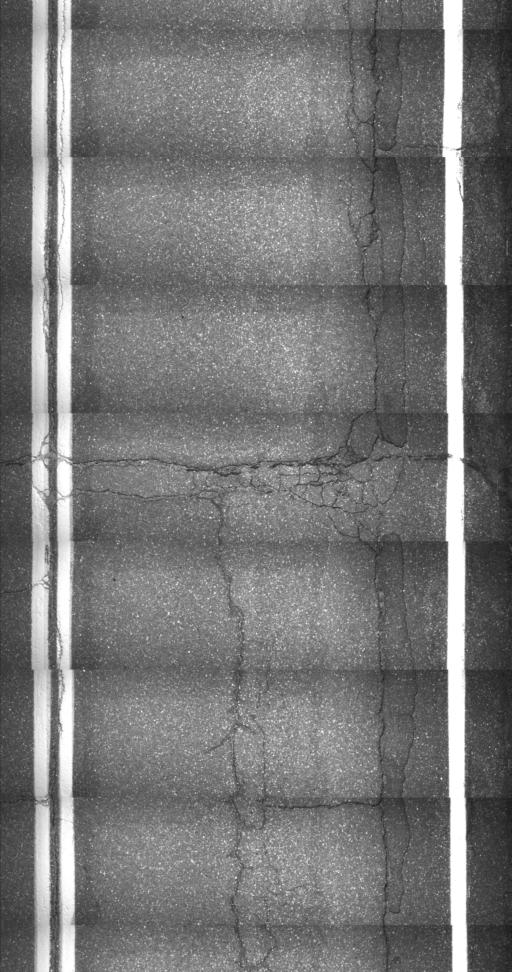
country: US
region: Vermont
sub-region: Caledonia County
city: St Johnsbury
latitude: 44.4268
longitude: -72.0446
